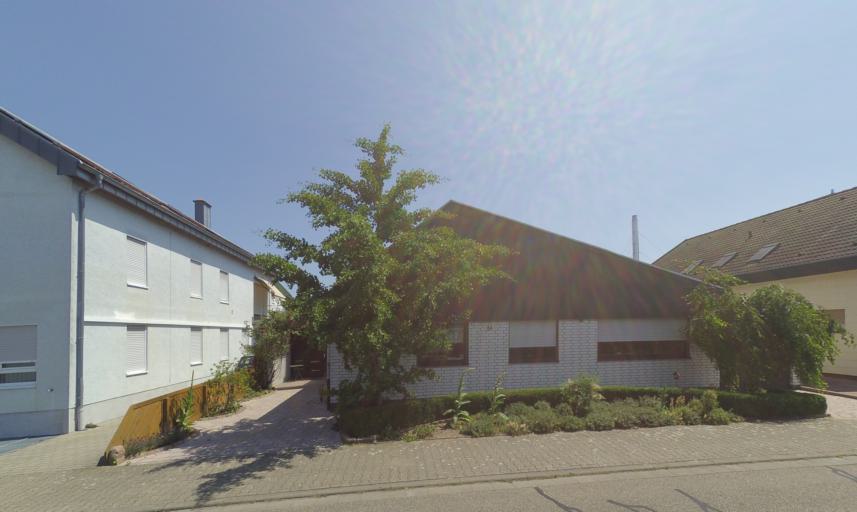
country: DE
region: Rheinland-Pfalz
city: Otterstadt
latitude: 49.3704
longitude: 8.4454
